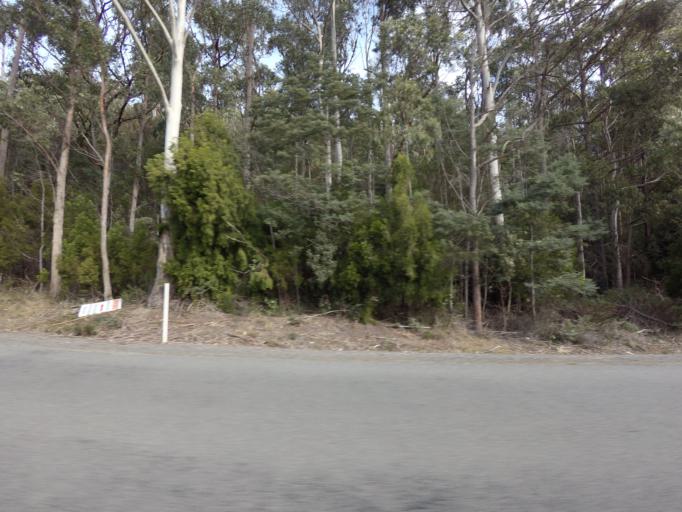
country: AU
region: Tasmania
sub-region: Clarence
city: Sandford
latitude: -43.1174
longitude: 147.7555
